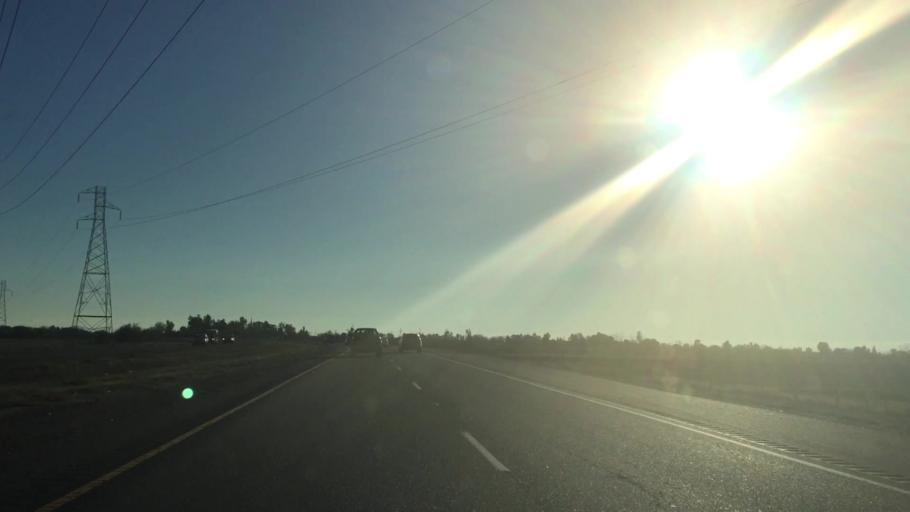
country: US
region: California
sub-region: Yuba County
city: Olivehurst
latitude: 39.0633
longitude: -121.5429
